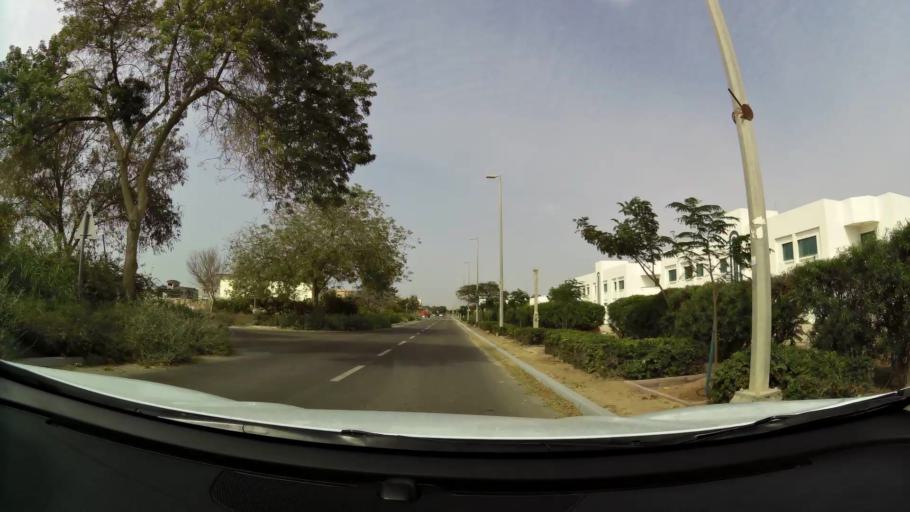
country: AE
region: Abu Dhabi
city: Abu Dhabi
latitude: 24.5697
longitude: 54.6931
